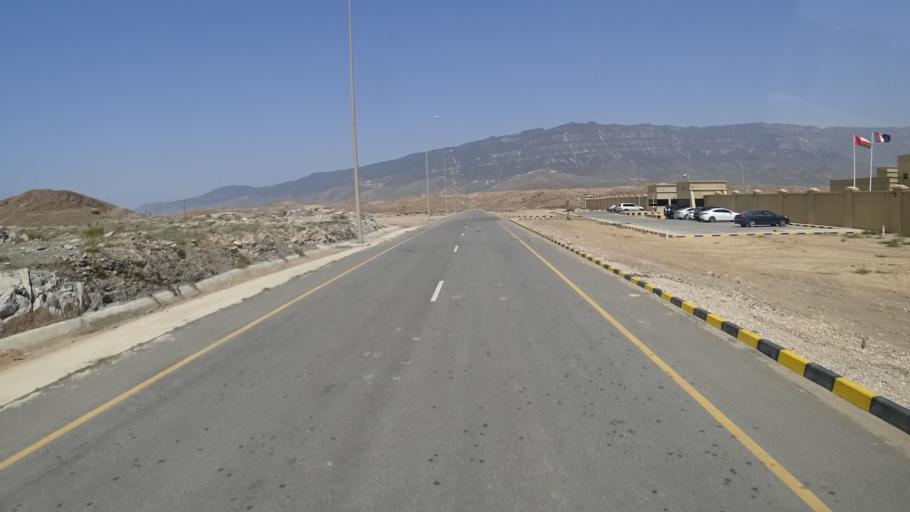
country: OM
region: Zufar
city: Salalah
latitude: 17.0097
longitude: 54.7005
